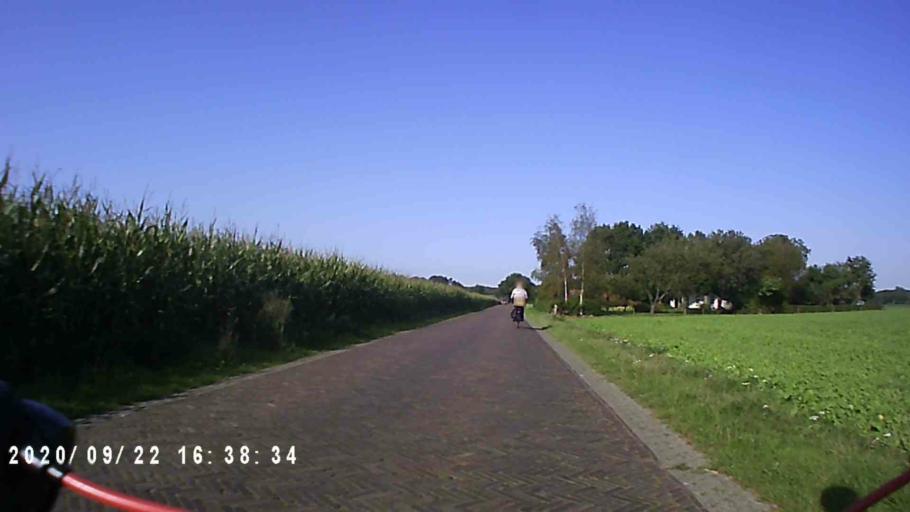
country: NL
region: Groningen
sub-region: Gemeente Leek
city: Leek
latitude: 53.1104
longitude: 6.4469
